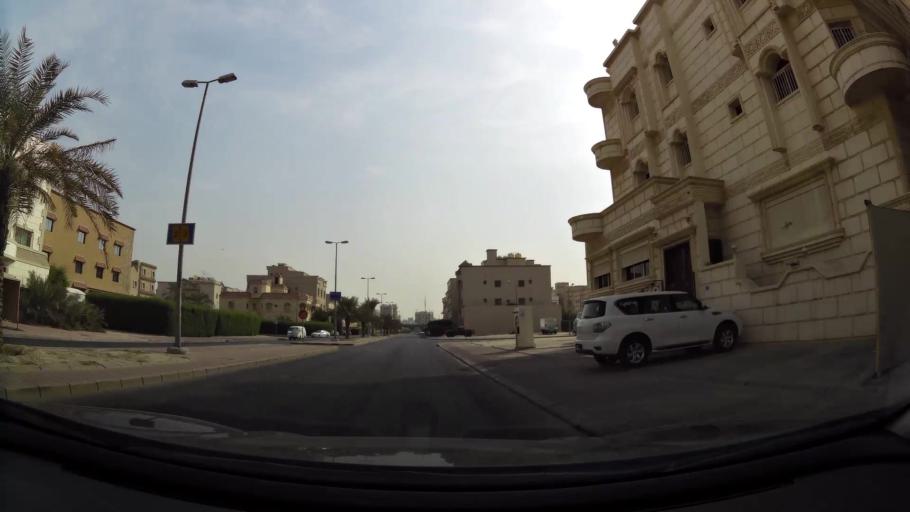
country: KW
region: Al Farwaniyah
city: Al Farwaniyah
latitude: 29.2711
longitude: 47.9396
